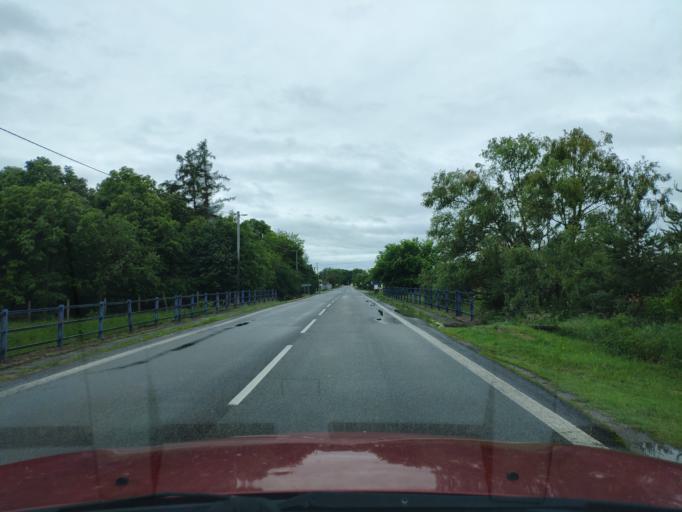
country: HU
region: Borsod-Abauj-Zemplen
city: Karcsa
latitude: 48.3970
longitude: 21.8073
